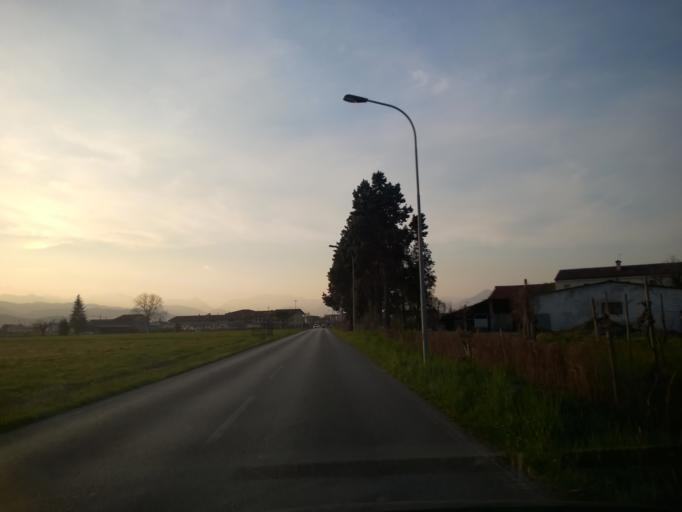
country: IT
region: Veneto
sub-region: Provincia di Vicenza
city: Caldogno-Rettorgole-Cresole
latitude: 45.6051
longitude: 11.5136
